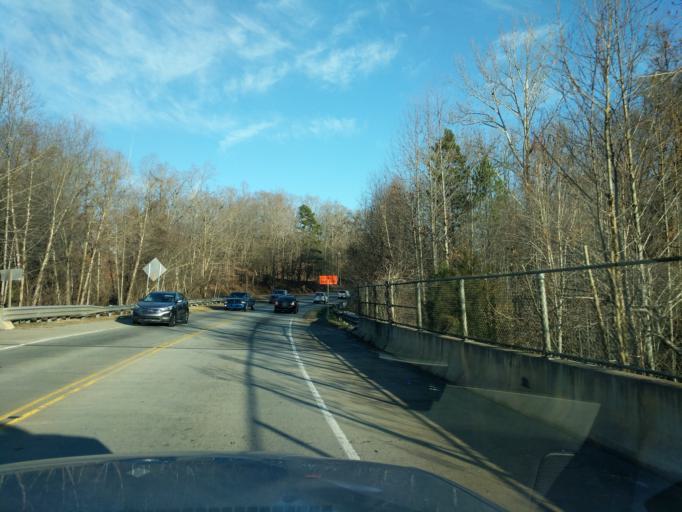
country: US
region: South Carolina
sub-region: Anderson County
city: Williamston
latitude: 34.6424
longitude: -82.4554
